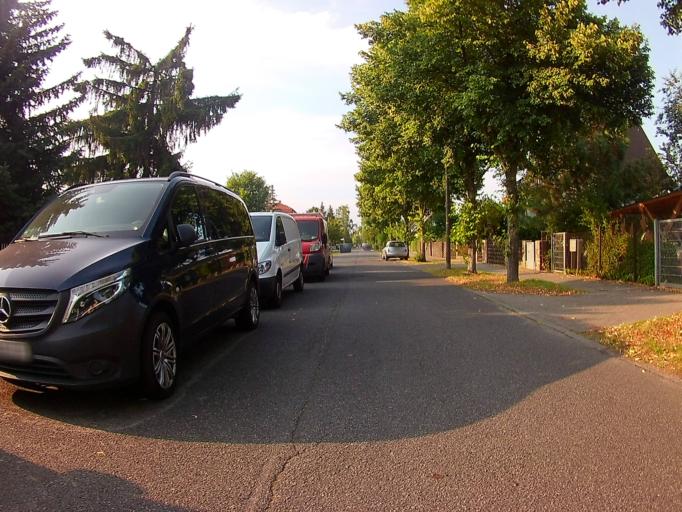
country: DE
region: Berlin
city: Biesdorf
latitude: 52.5248
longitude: 13.5498
